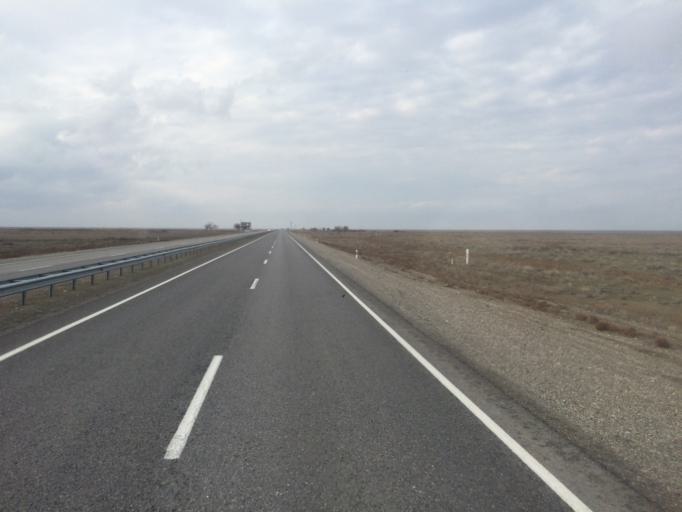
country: KZ
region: Ongtustik Qazaqstan
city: Turkestan
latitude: 43.5242
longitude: 67.7969
